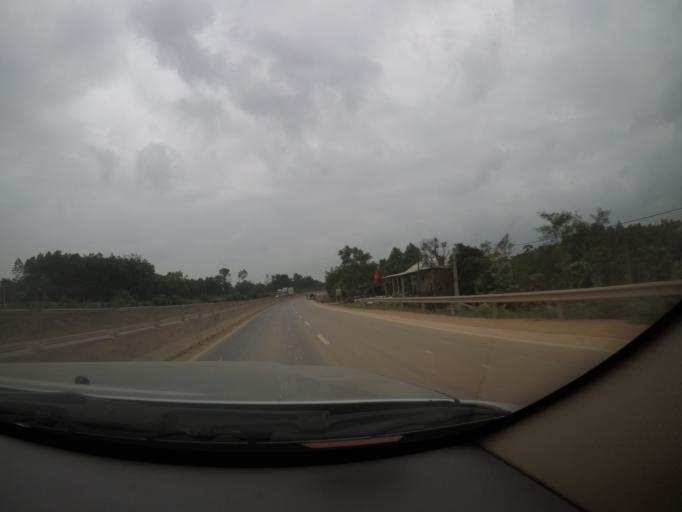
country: VN
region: Thua Thien-Hue
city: Phong Dien
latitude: 16.6161
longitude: 107.3126
